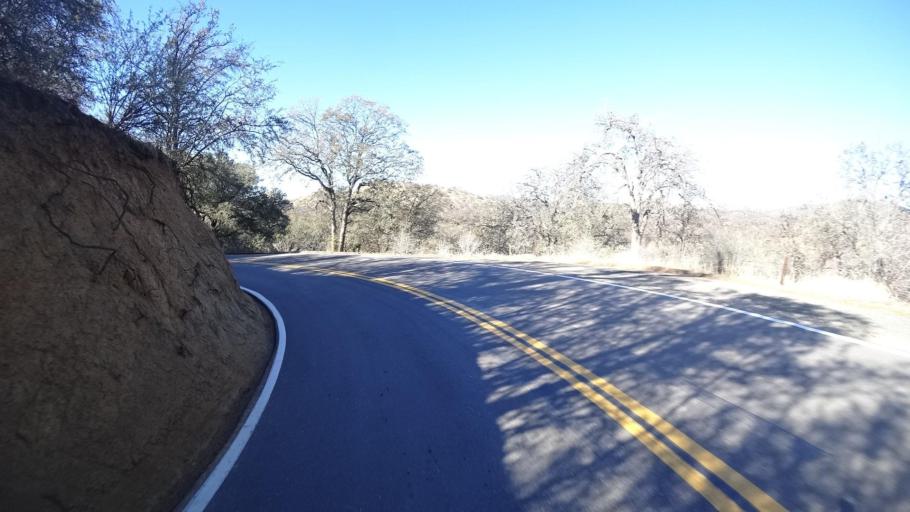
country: US
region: California
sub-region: Kern County
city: Alta Sierra
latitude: 35.7376
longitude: -118.6538
